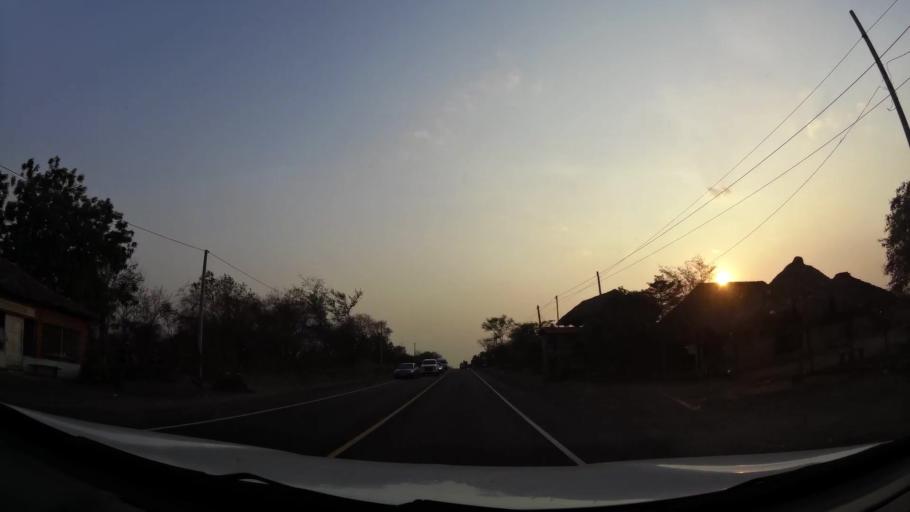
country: NI
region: Leon
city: La Paz Centro
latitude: 12.3369
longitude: -86.6638
